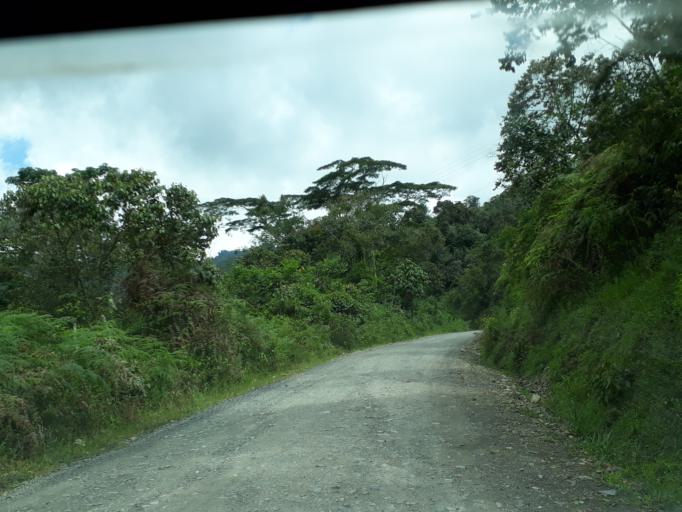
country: CO
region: Cundinamarca
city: Pacho
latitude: 5.2621
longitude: -74.1912
